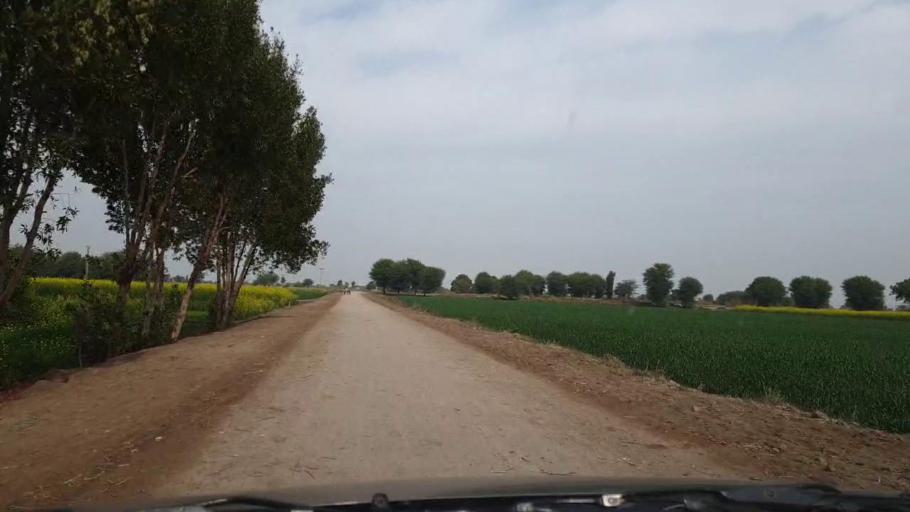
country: PK
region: Sindh
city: Sanghar
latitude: 26.0973
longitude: 68.8815
